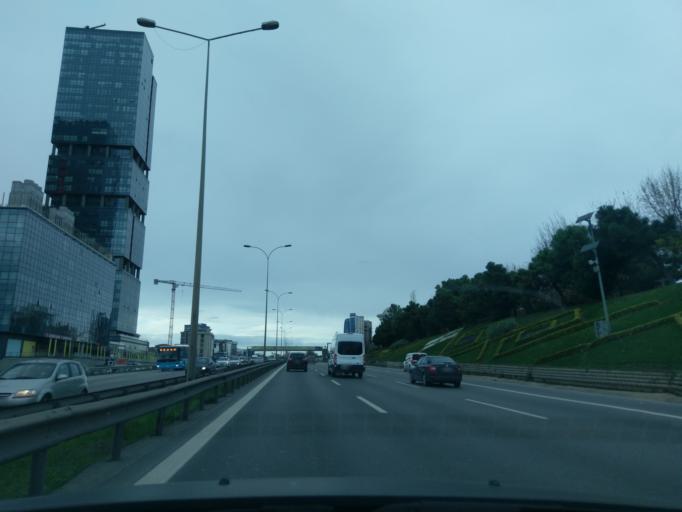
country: TR
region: Istanbul
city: Maltepe
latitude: 40.9222
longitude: 29.1611
